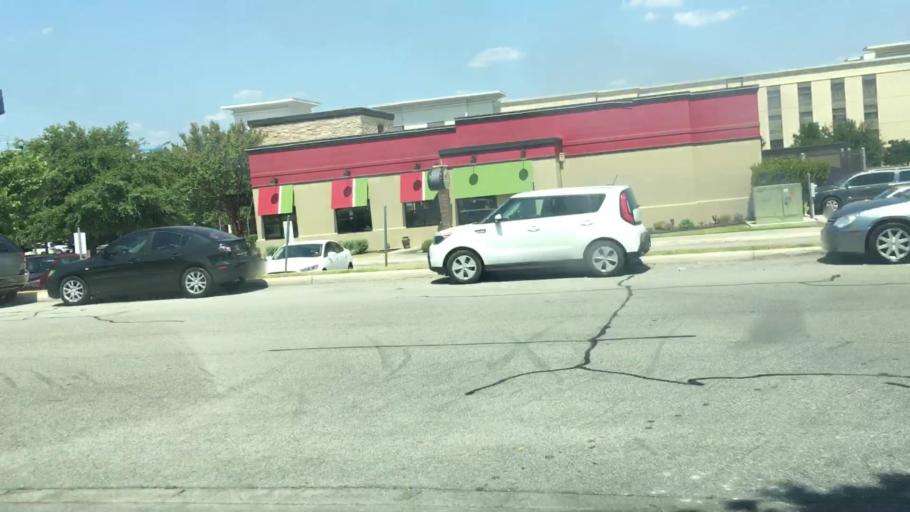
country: US
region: Texas
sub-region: Bexar County
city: Selma
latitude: 29.6001
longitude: -98.2749
